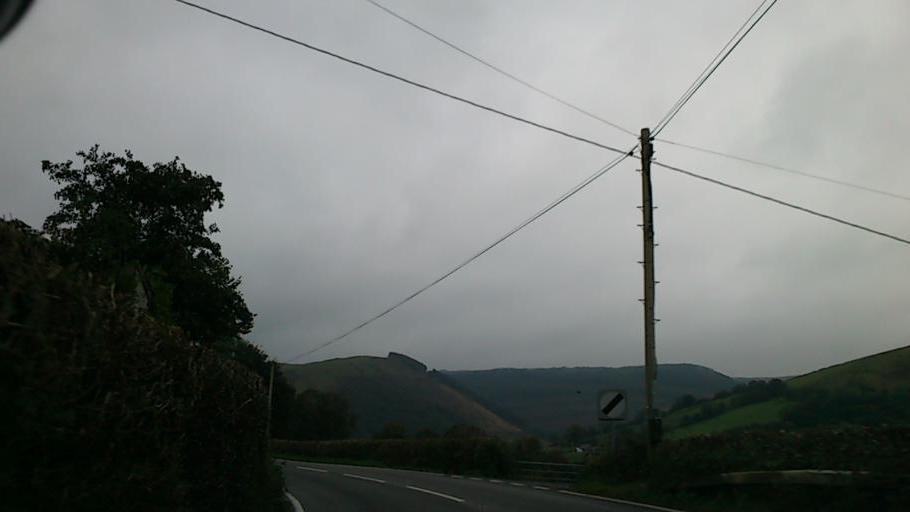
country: GB
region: Wales
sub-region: Gwynedd
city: Corris
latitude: 52.6990
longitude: -3.6546
